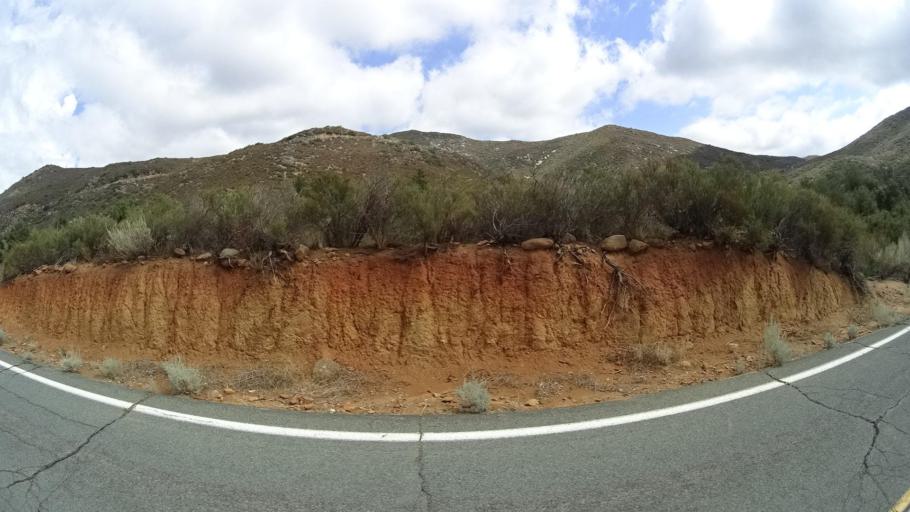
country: US
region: California
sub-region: San Diego County
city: Pine Valley
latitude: 32.7796
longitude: -116.4495
